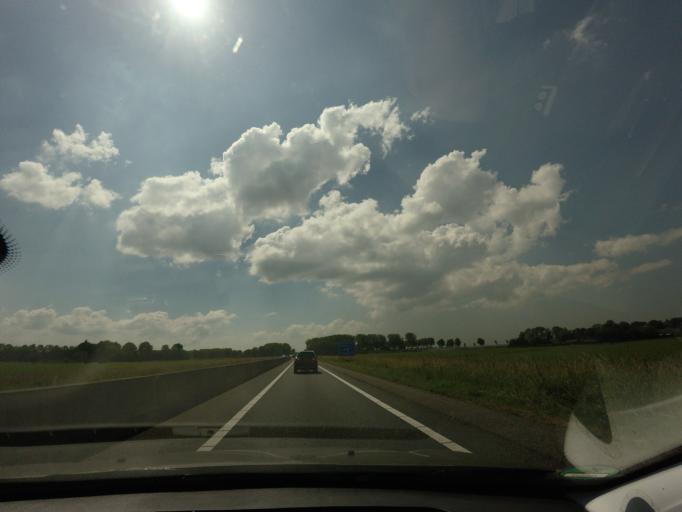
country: NL
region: South Holland
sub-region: Gemeente Hellevoetsluis
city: Nieuwenhoorn
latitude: 51.8634
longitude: 4.1638
